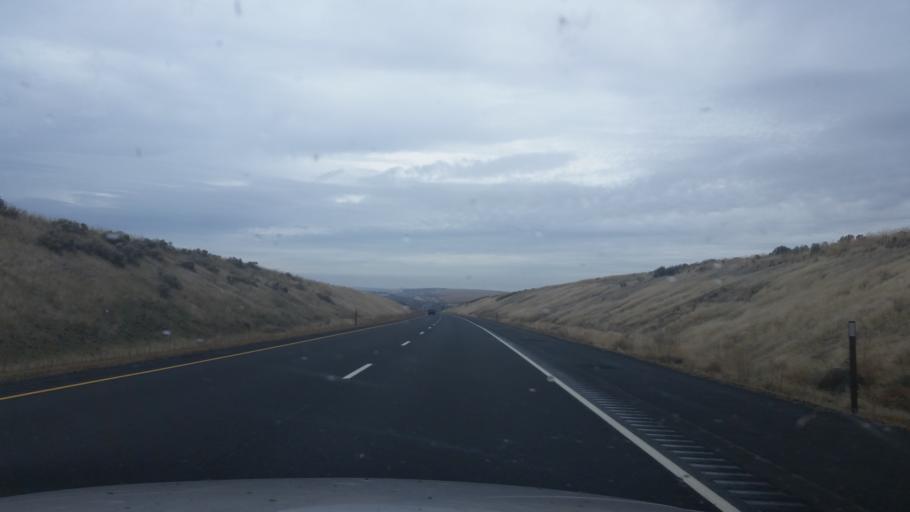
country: US
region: Washington
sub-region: Grant County
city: Warden
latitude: 47.0871
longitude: -118.8592
